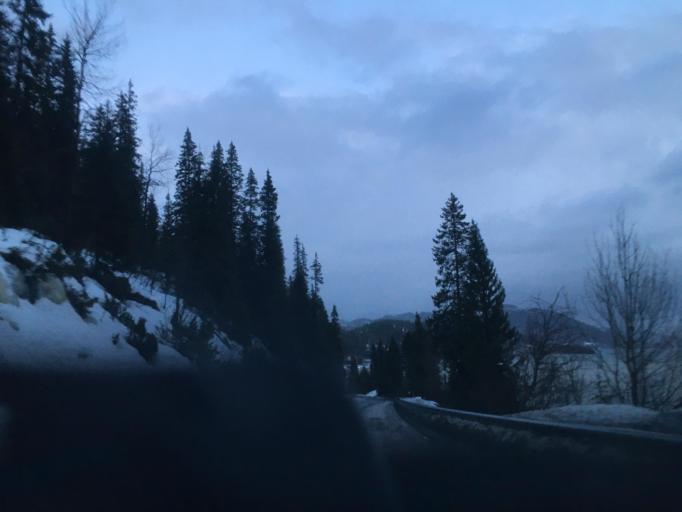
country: NO
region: Nordland
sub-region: Rana
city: Hauknes
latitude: 66.2986
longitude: 13.9261
